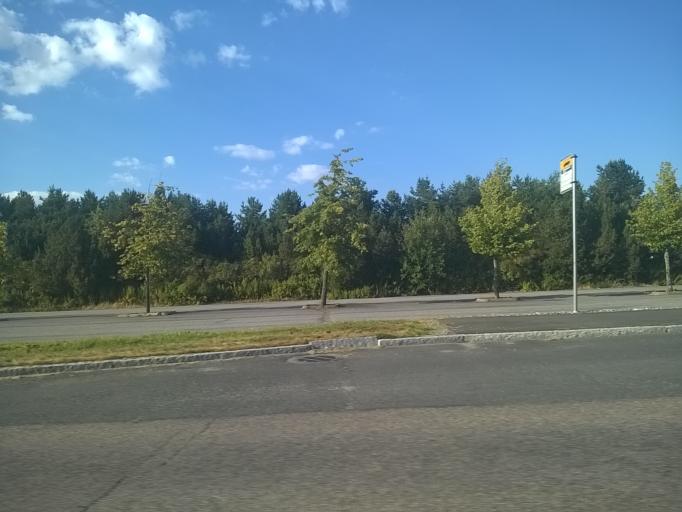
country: FI
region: Pirkanmaa
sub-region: Tampere
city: Tampere
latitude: 61.4627
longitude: 23.7524
